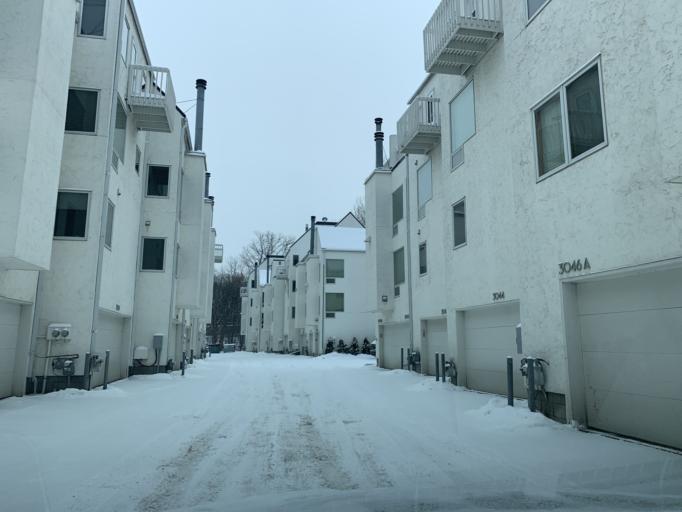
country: US
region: Minnesota
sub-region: Hennepin County
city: Saint Louis Park
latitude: 44.9475
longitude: -93.3258
